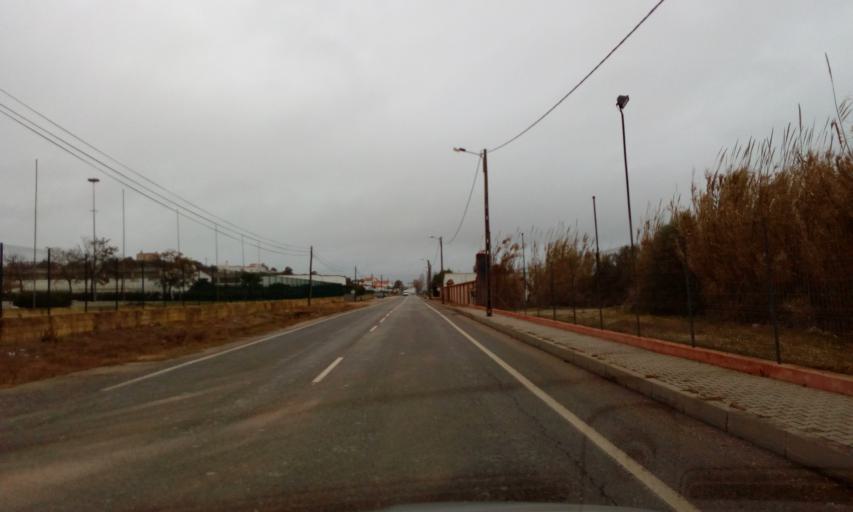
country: PT
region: Faro
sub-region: Albufeira
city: Guia
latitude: 37.1585
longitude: -8.2925
